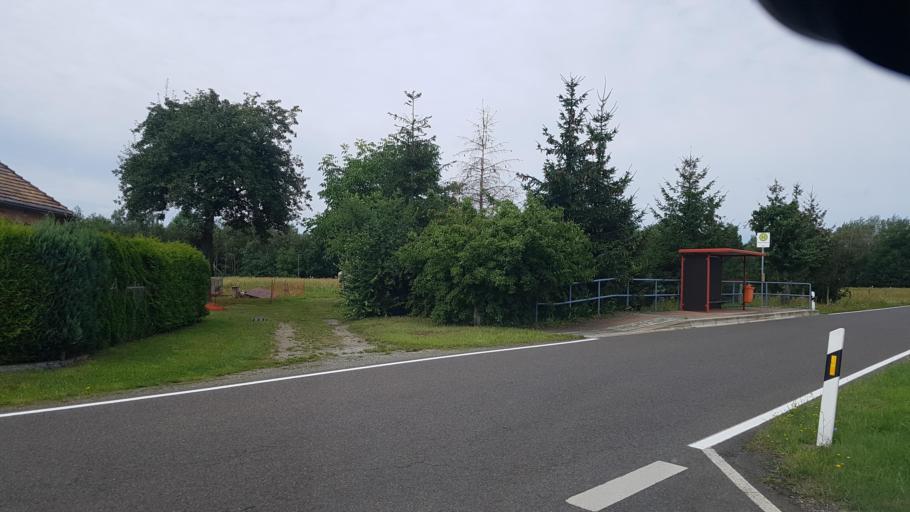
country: DE
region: Brandenburg
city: Spremberg
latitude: 51.5953
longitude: 14.3429
